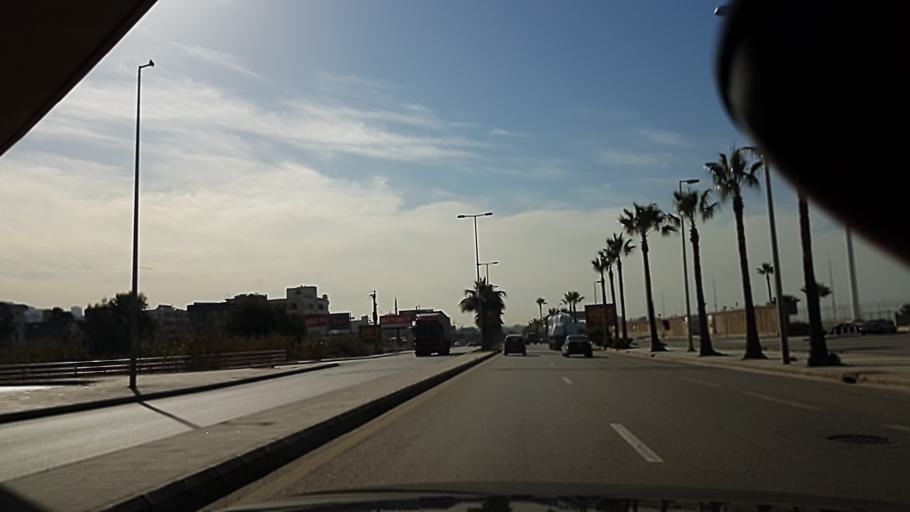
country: LB
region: Liban-Sud
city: Sidon
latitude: 33.5873
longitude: 35.3866
